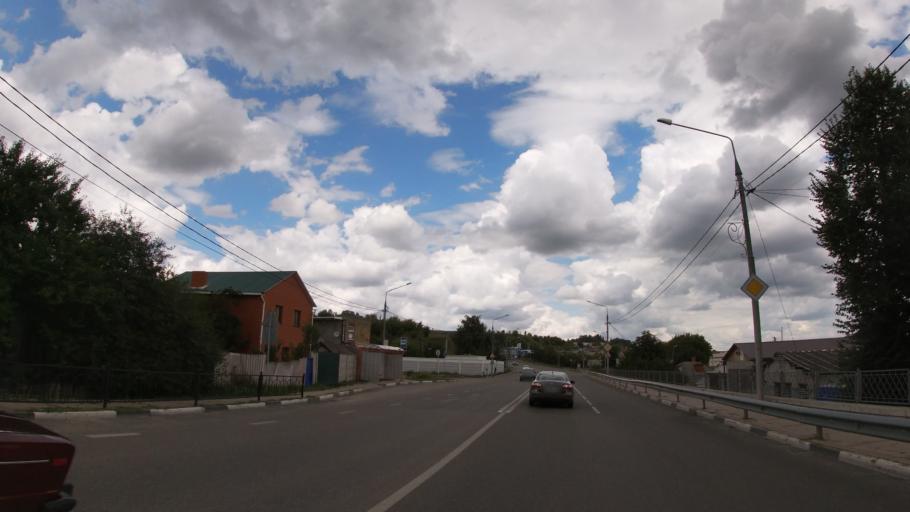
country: RU
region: Belgorod
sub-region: Belgorodskiy Rayon
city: Belgorod
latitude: 50.6076
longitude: 36.6129
